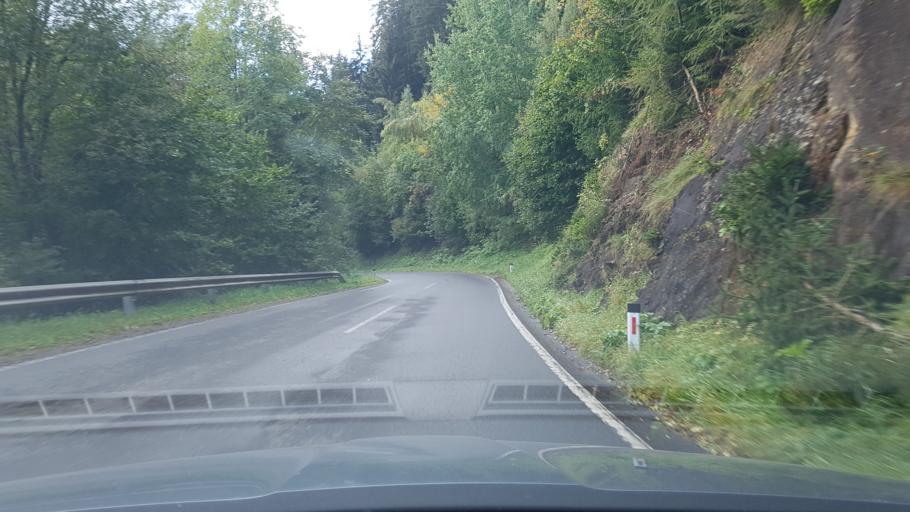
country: AT
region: Styria
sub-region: Politischer Bezirk Murau
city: Schoder
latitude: 47.1940
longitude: 14.1214
